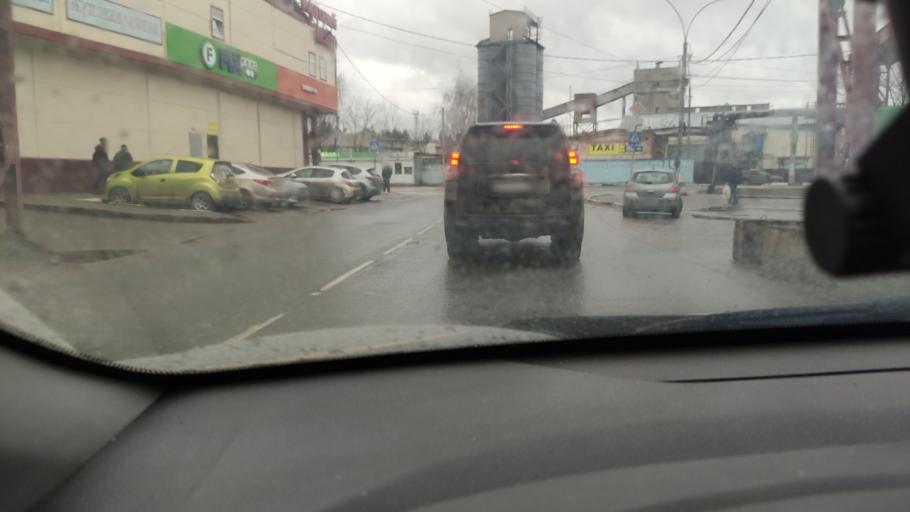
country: RU
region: Moskovskaya
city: Selyatino
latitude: 55.5153
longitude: 36.9722
